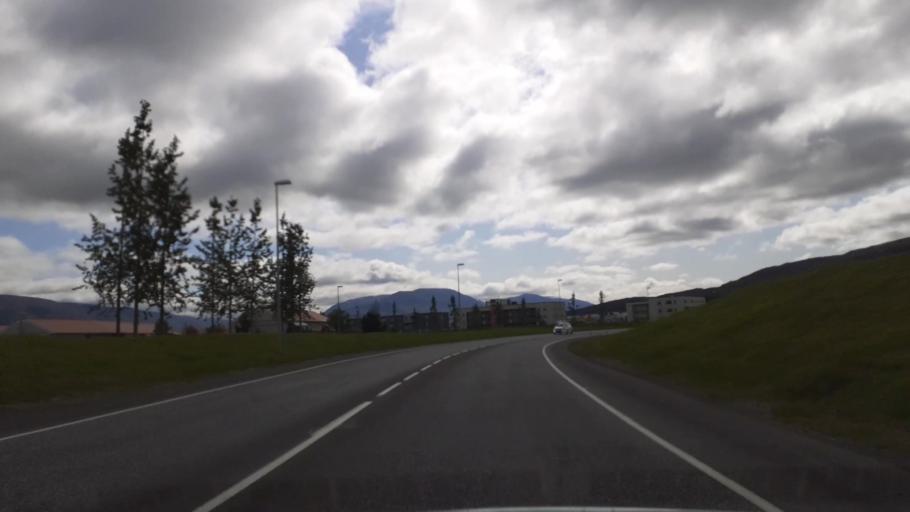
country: IS
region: Northeast
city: Akureyri
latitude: 65.6712
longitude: -18.1076
